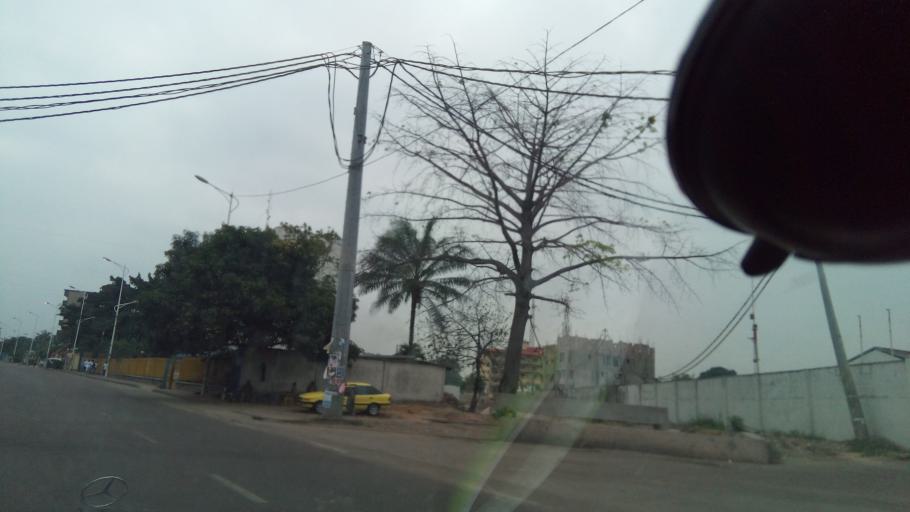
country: CD
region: Kinshasa
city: Kinshasa
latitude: -4.3199
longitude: 15.2757
